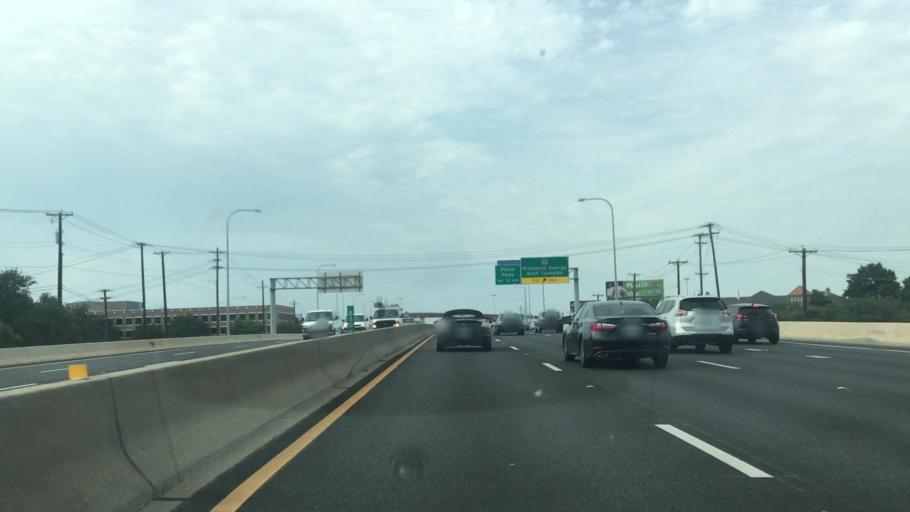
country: US
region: Texas
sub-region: Dallas County
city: Addison
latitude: 33.0062
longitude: -96.8291
